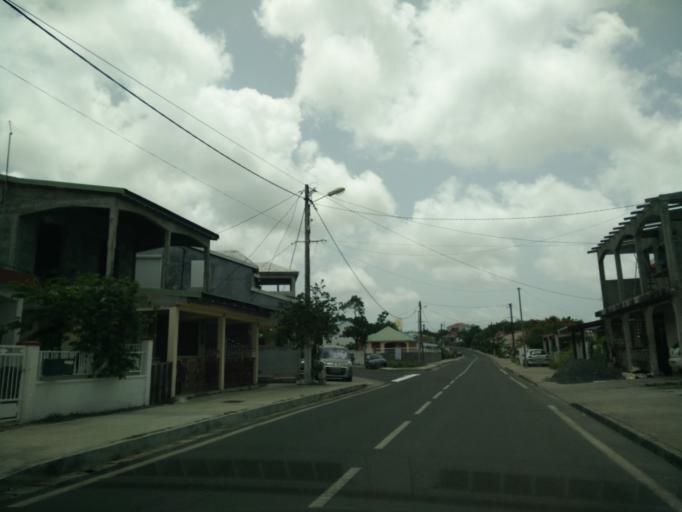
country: GP
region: Guadeloupe
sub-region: Guadeloupe
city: Port-Louis
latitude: 16.4192
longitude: -61.5285
